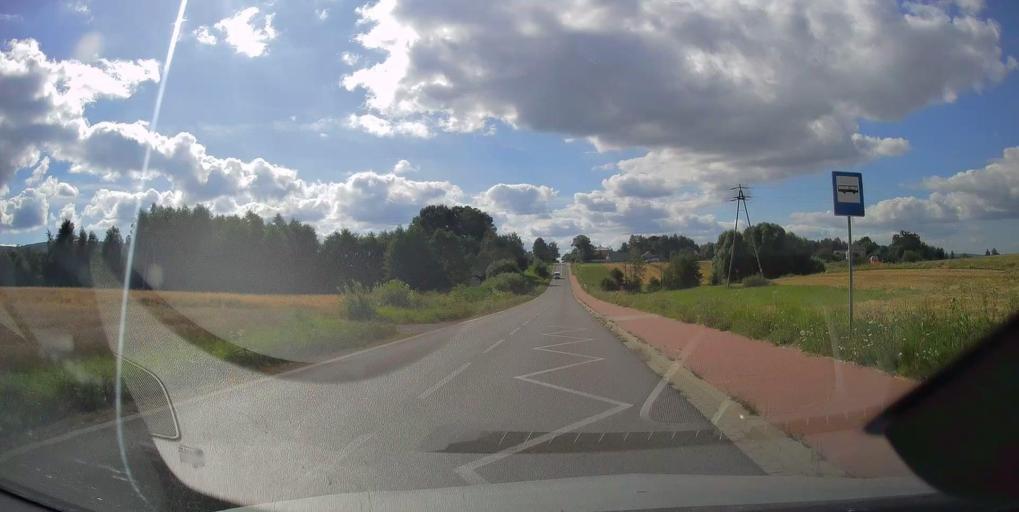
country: PL
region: Swietokrzyskie
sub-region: Powiat kielecki
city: Nowa Slupia
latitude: 50.8816
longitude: 21.0570
